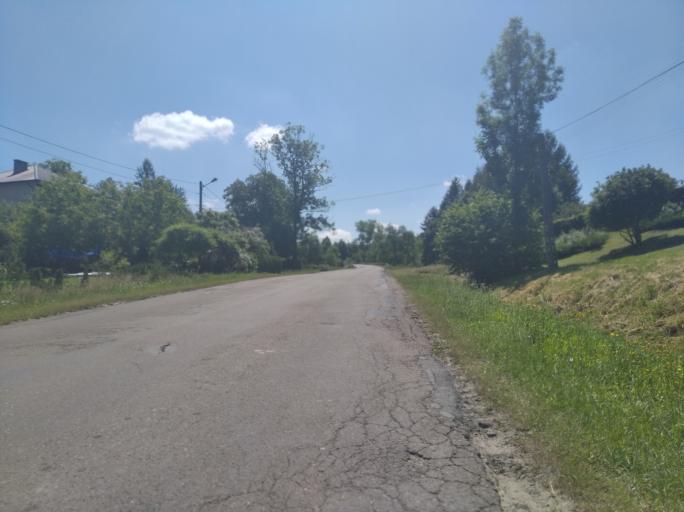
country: PL
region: Subcarpathian Voivodeship
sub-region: Powiat brzozowski
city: Jablonka
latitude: 49.6915
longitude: 22.1149
